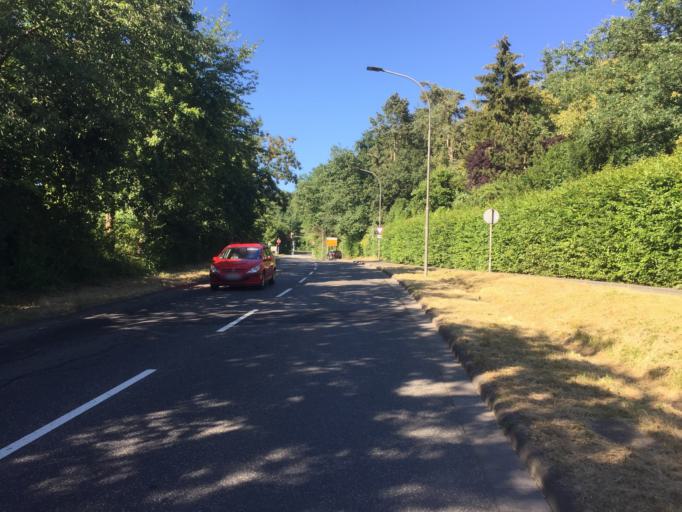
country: DE
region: Hesse
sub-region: Regierungsbezirk Giessen
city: Giessen
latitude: 50.5484
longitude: 8.7227
